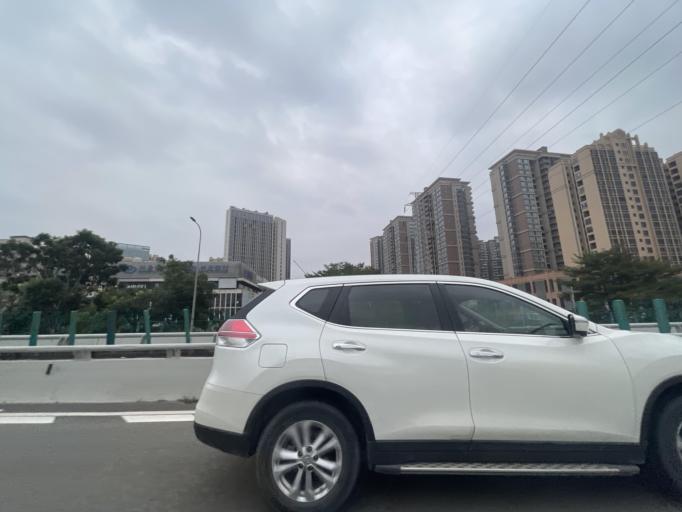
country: CN
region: Guangdong
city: Humen
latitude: 22.8064
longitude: 113.6834
